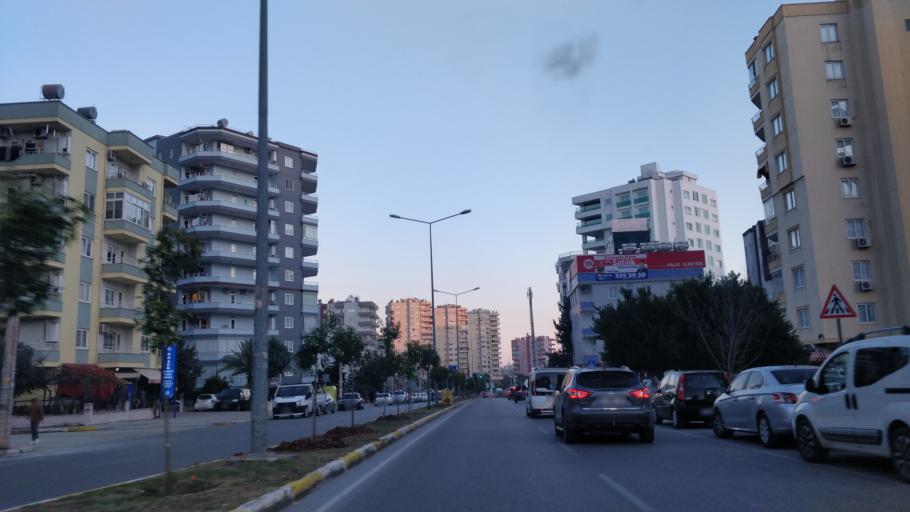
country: TR
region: Mersin
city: Mercin
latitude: 36.7919
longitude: 34.5889
